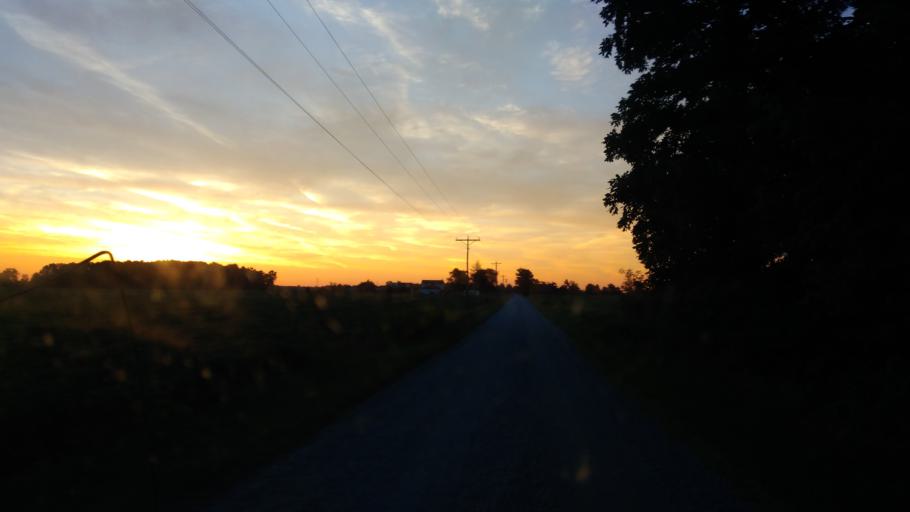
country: US
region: Indiana
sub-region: Wells County
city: Bluffton
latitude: 40.6845
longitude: -85.1195
